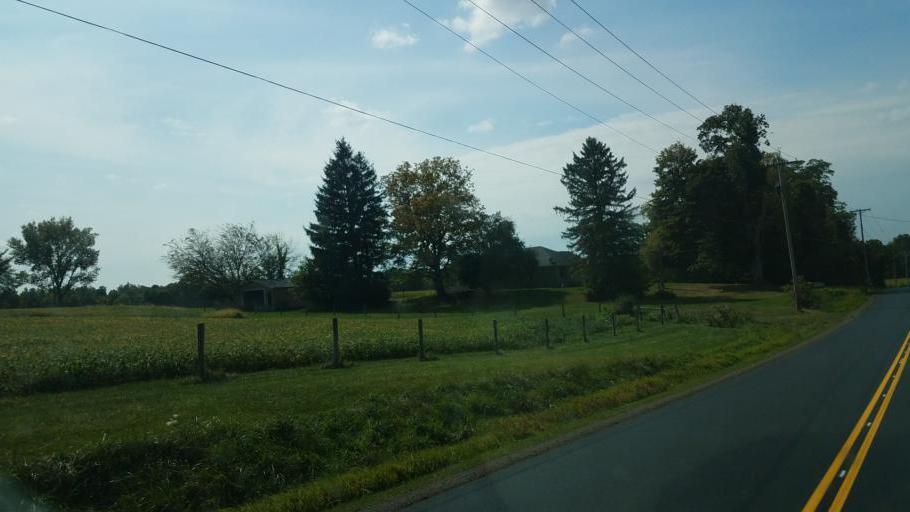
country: US
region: Ohio
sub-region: Knox County
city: Fredericktown
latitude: 40.4039
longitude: -82.6206
